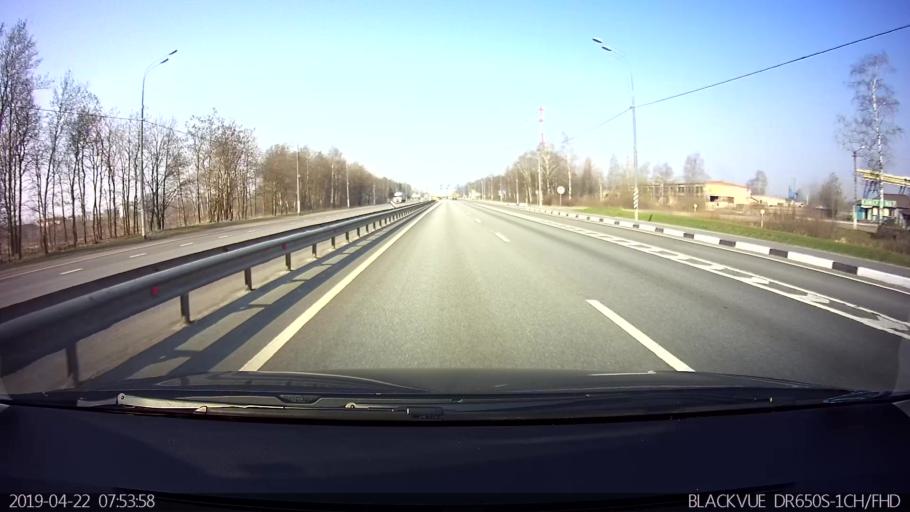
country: RU
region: Smolensk
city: Safonovo
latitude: 55.1430
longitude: 33.2658
